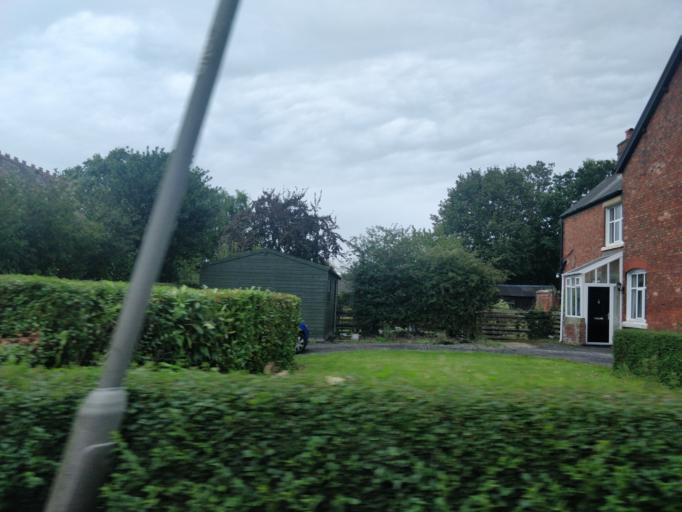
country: GB
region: England
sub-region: Lancashire
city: Ormskirk
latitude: 53.6117
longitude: -2.9175
